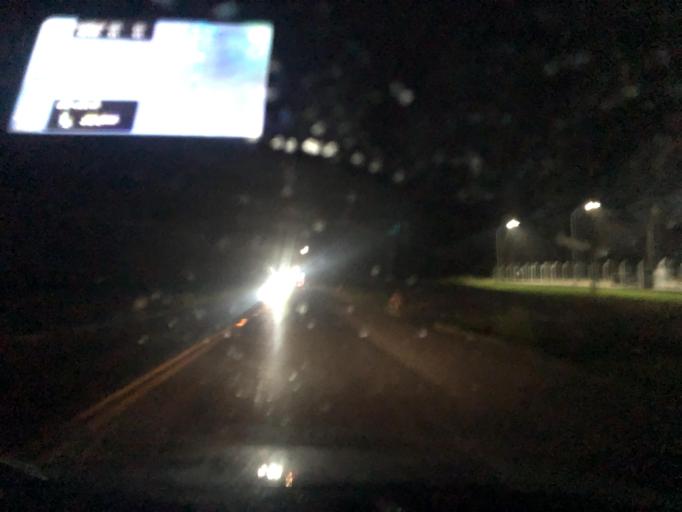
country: BR
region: Santa Catarina
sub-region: Guaramirim
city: Guaramirim
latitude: -26.4532
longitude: -48.9100
